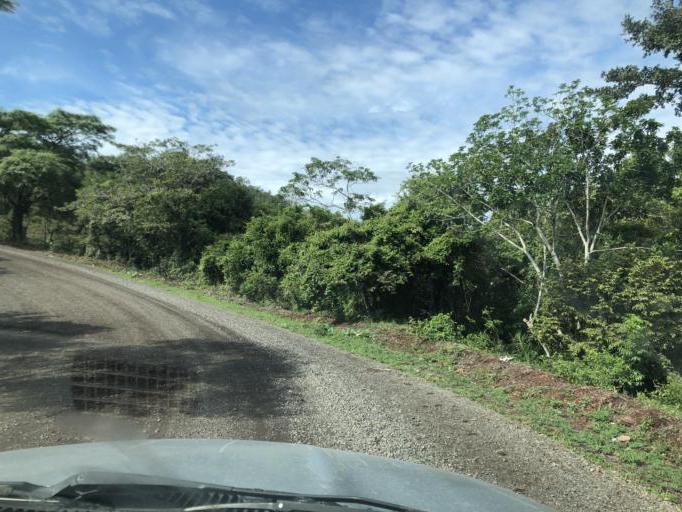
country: MX
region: Veracruz
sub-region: Alto Lucero de Gutierrez Barrios
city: Palma Sola
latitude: 19.7833
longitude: -96.5547
